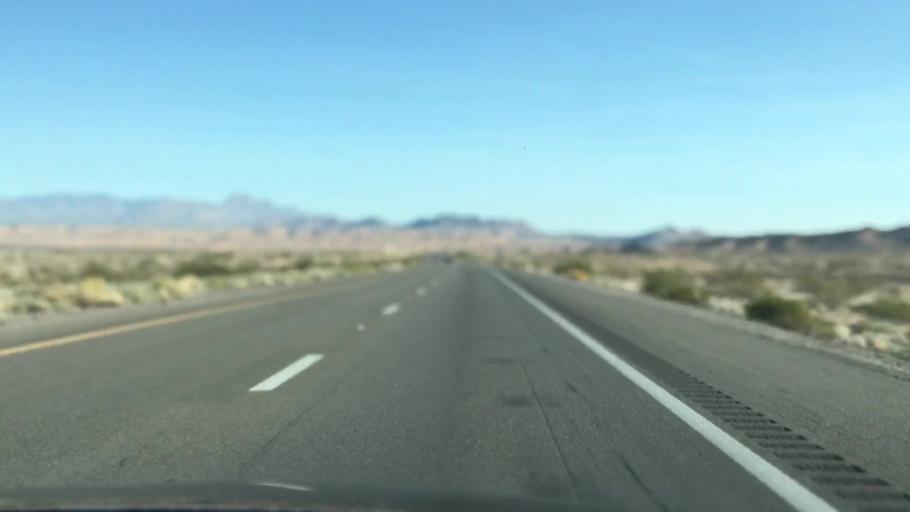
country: US
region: Nevada
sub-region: Clark County
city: Moapa Town
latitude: 36.6408
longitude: -114.5946
